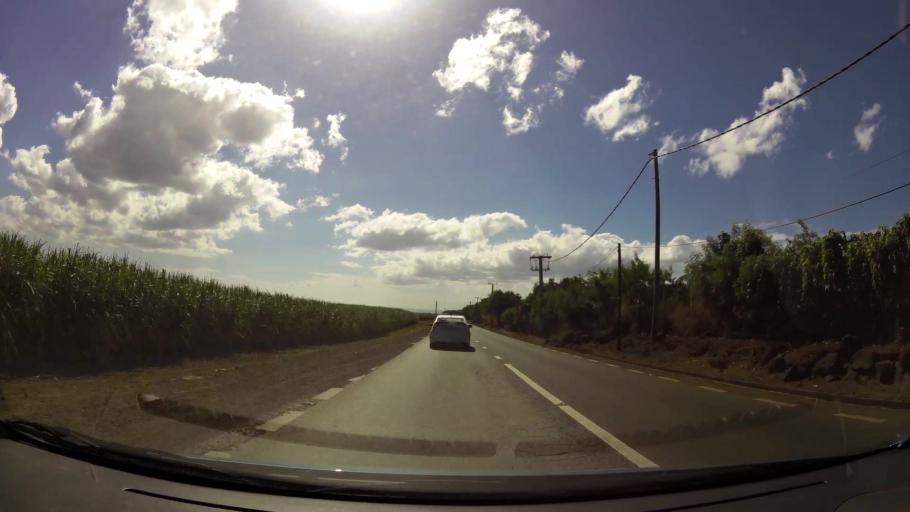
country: MU
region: Black River
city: Gros Cailloux
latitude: -20.2326
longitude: 57.4254
